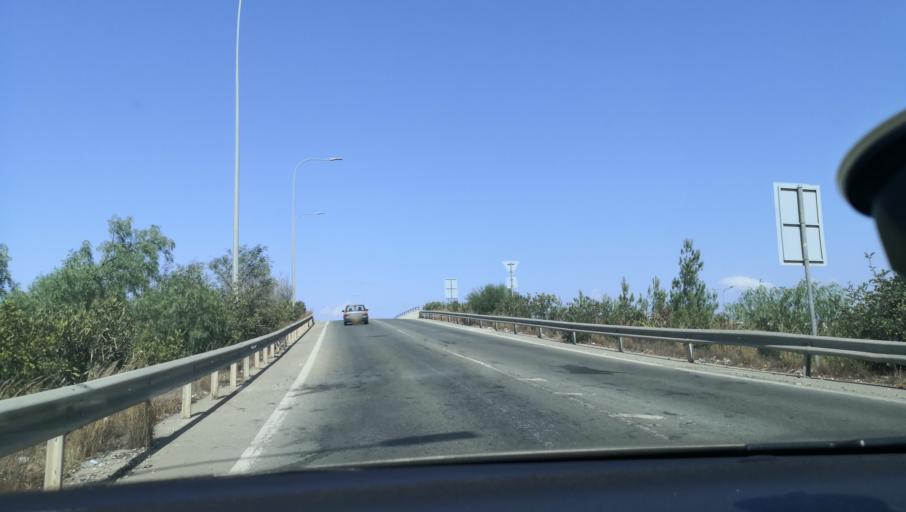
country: CY
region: Lefkosia
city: Kokkinotrimithia
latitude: 35.1596
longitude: 33.2029
